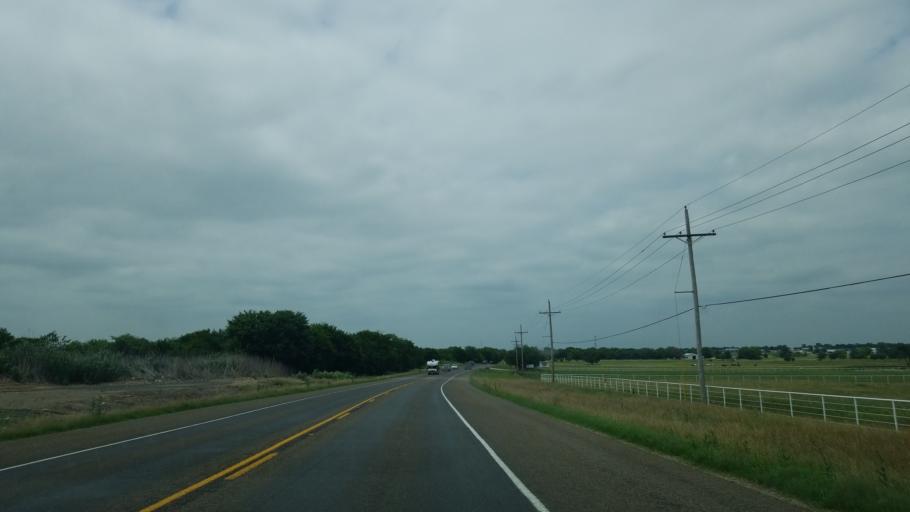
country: US
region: Texas
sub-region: Denton County
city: Aubrey
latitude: 33.3314
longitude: -96.9705
